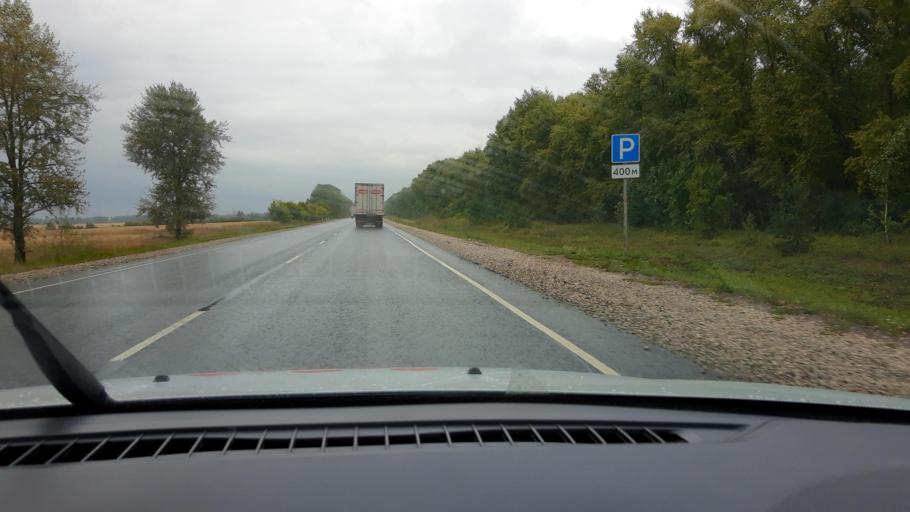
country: RU
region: Chuvashia
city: Yantikovo
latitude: 55.7896
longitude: 47.7025
